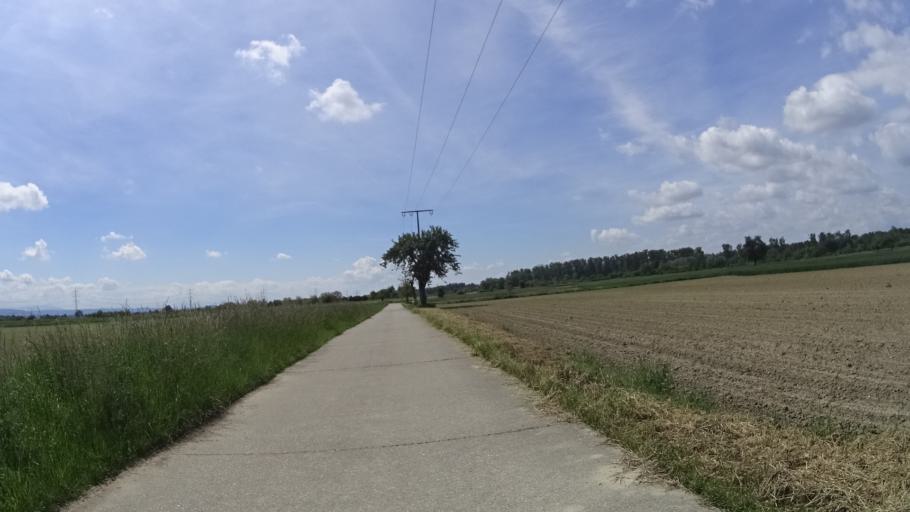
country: DE
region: Baden-Wuerttemberg
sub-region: Freiburg Region
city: Schwanau
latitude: 48.3780
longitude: 7.7536
